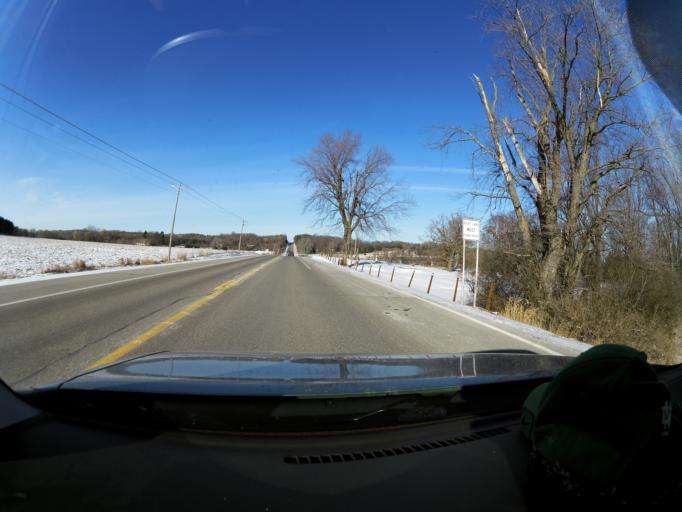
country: US
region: Minnesota
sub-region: Washington County
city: Afton
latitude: 44.9155
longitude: -92.8626
